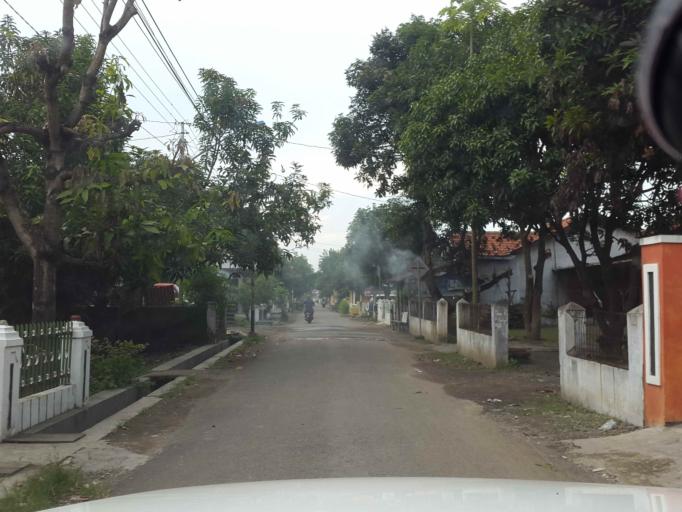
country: ID
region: Central Java
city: Tegal
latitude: -6.8948
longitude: 109.1260
